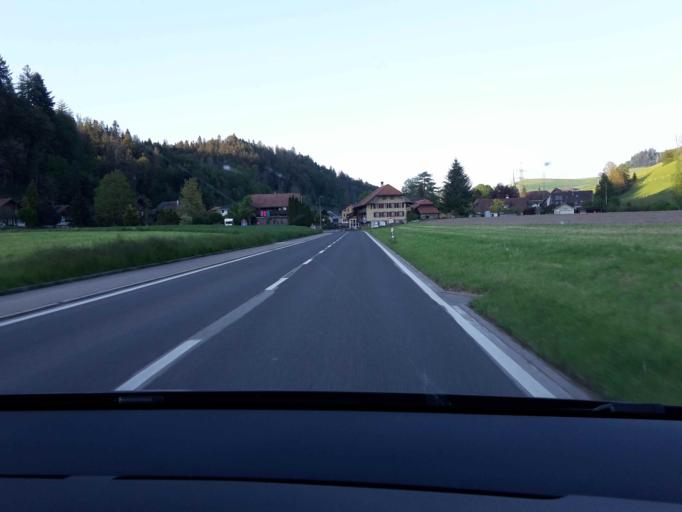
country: CH
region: Bern
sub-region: Emmental District
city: Lutzelfluh
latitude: 47.0230
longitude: 7.6686
